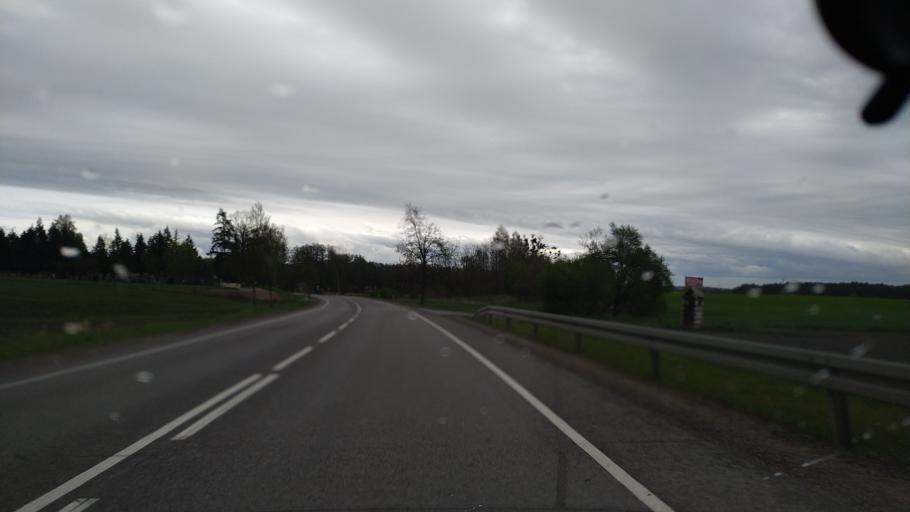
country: PL
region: Pomeranian Voivodeship
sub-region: Powiat starogardzki
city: Zblewo
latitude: 53.9301
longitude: 18.3238
